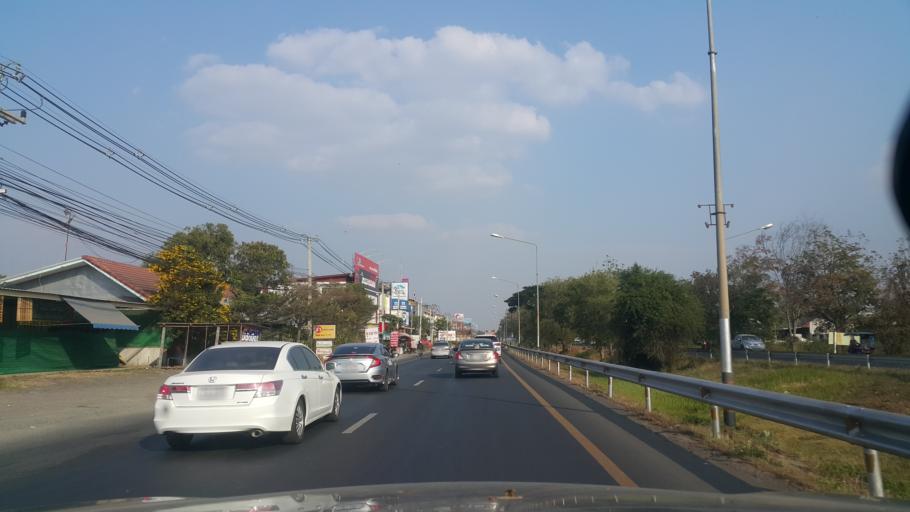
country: TH
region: Buriram
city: Nang Rong
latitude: 14.6332
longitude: 102.8052
